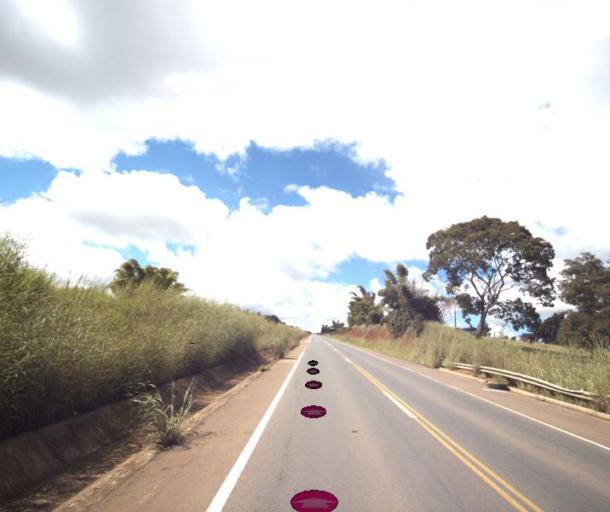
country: BR
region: Goias
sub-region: Anapolis
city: Anapolis
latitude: -16.2170
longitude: -49.0157
